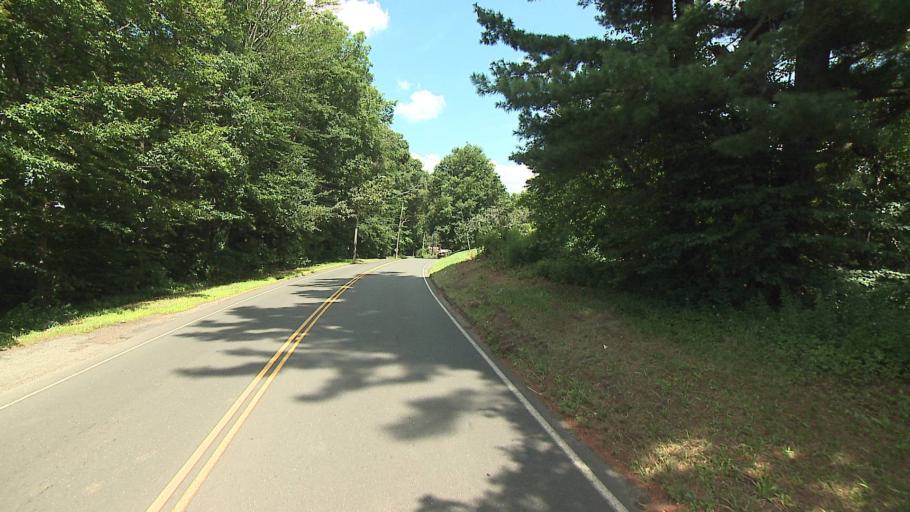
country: US
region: Connecticut
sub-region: Fairfield County
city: Shelton
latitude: 41.3189
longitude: -73.1090
